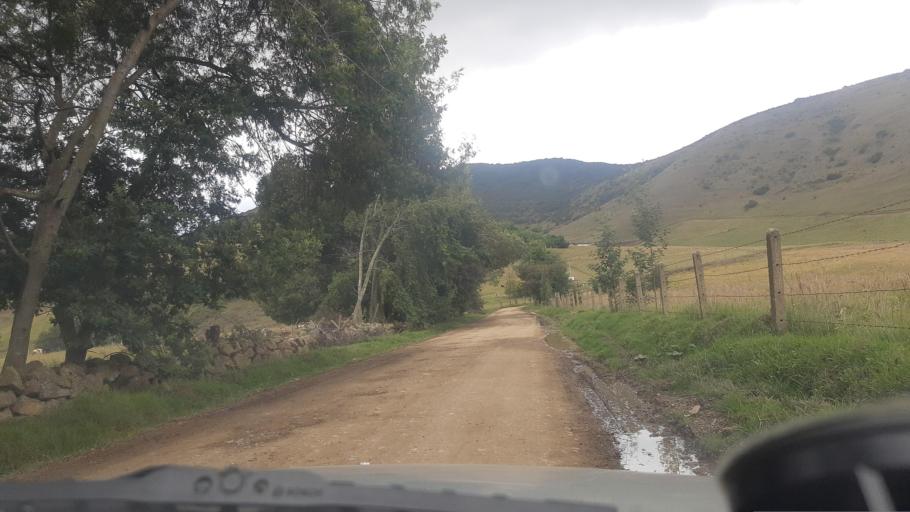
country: CO
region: Cundinamarca
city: Suesca
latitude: 5.1549
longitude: -73.7984
